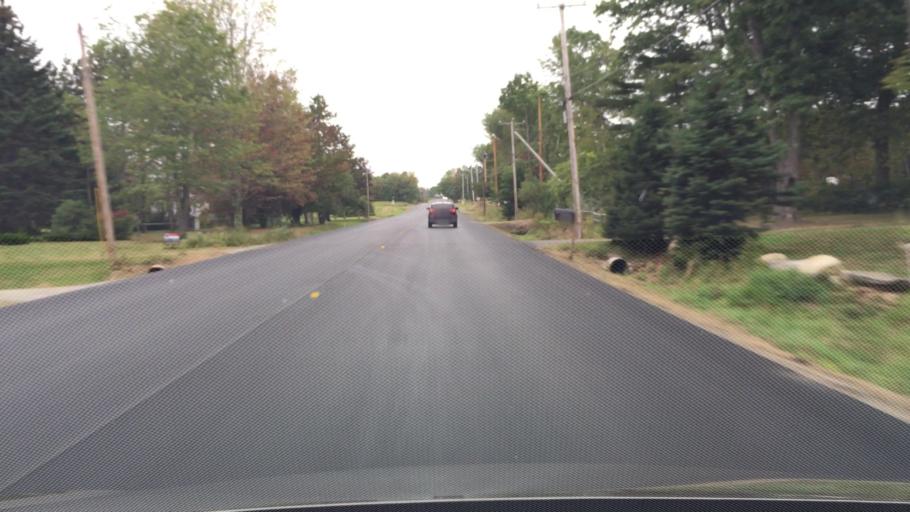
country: US
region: Maine
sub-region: Waldo County
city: Belfast
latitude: 44.4118
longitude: -69.0693
